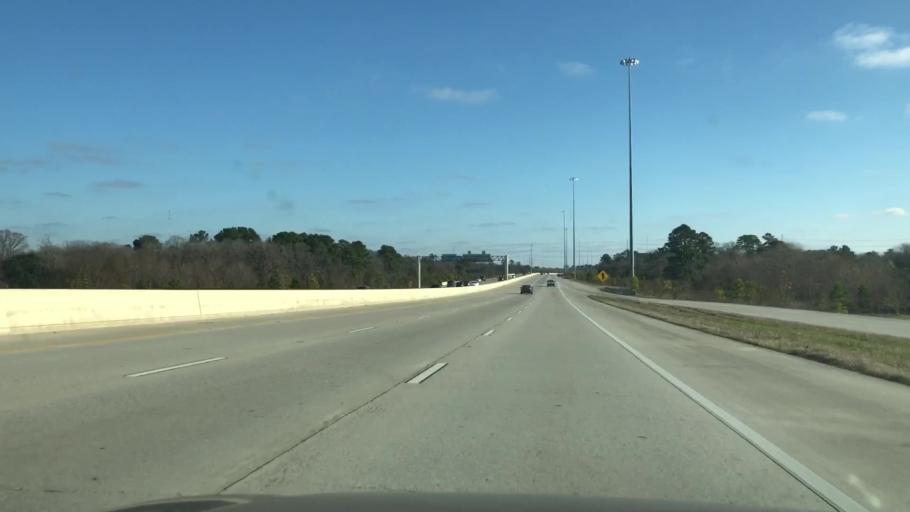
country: US
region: Texas
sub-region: Harris County
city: Jacinto City
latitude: 29.7856
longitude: -95.2447
